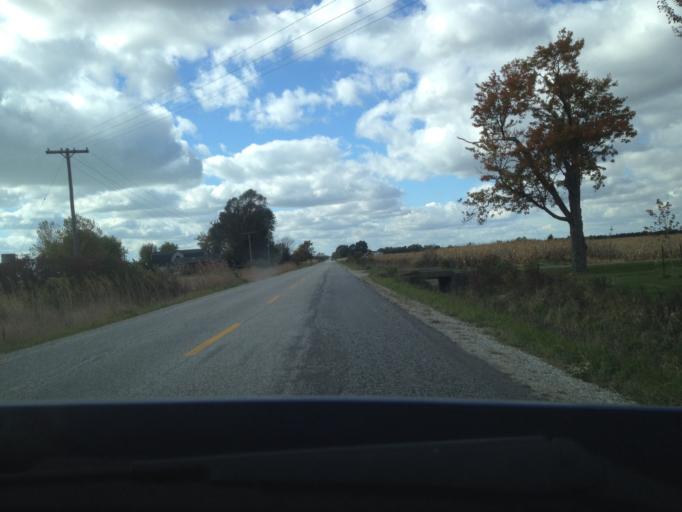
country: US
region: Michigan
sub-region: Wayne County
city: Grosse Pointe
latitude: 42.0316
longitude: -82.5372
